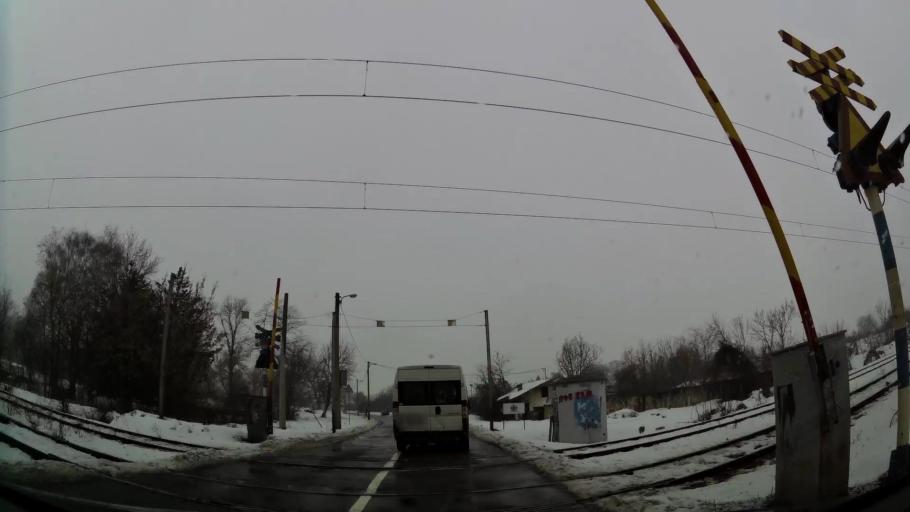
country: RS
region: Central Serbia
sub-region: Belgrade
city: Zemun
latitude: 44.8668
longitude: 20.3212
